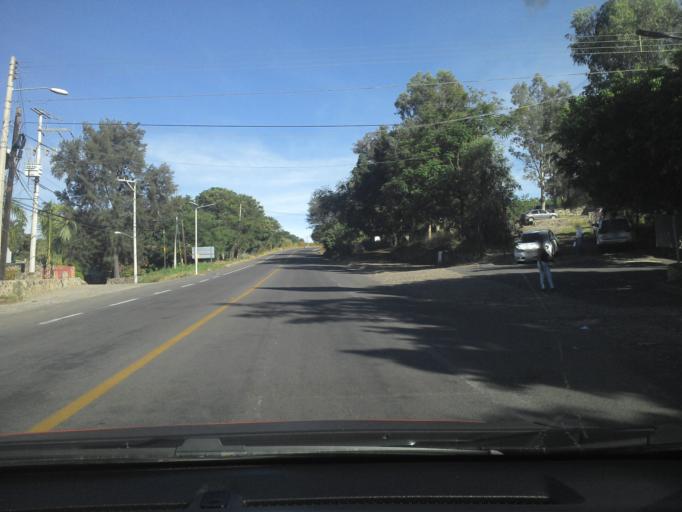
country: MX
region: Jalisco
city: Teuchitlan
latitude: 20.6805
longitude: -103.8448
